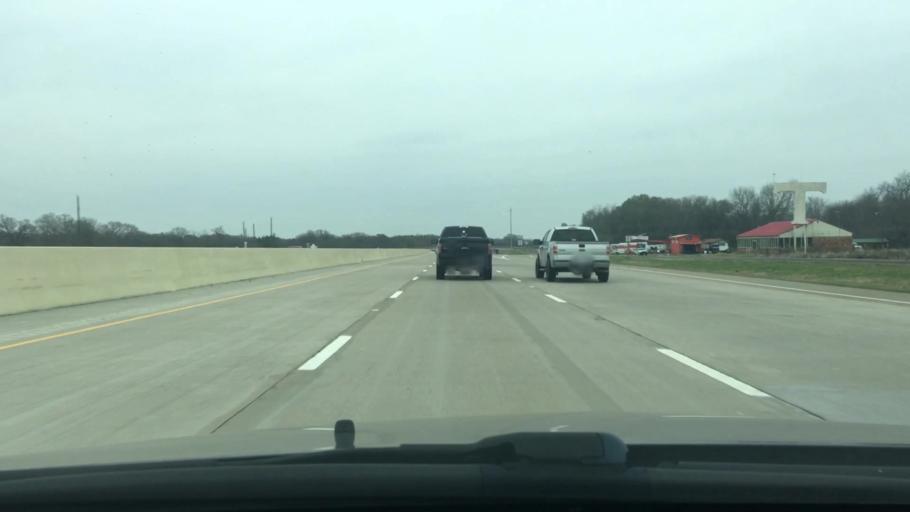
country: US
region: Texas
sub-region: Navarro County
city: Corsicana
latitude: 31.9677
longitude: -96.4215
